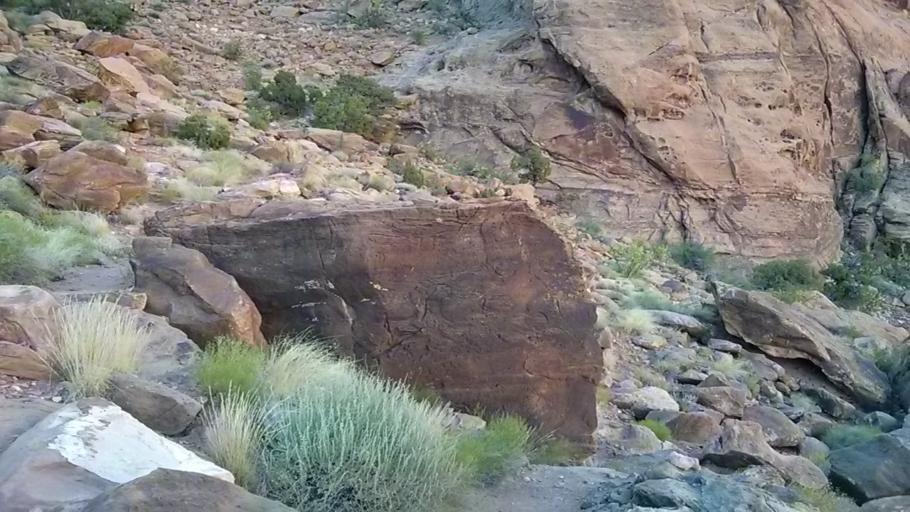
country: US
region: Utah
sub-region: Grand County
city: Moab
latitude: 38.4321
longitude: -109.9487
